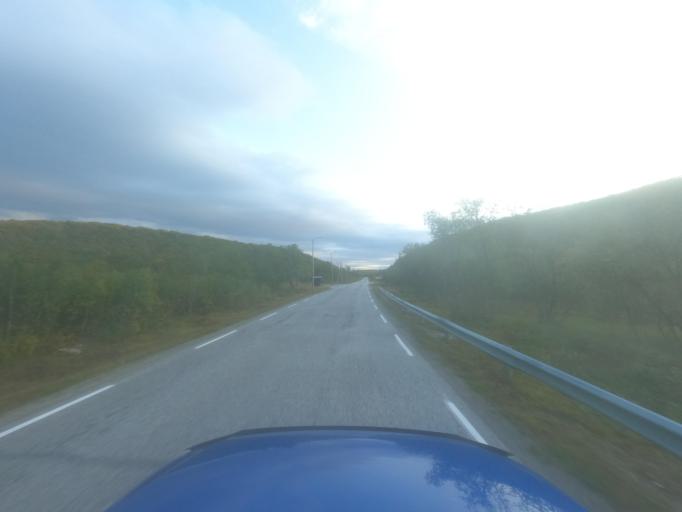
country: NO
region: Finnmark Fylke
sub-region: Porsanger
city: Lakselv
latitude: 70.2862
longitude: 25.0732
